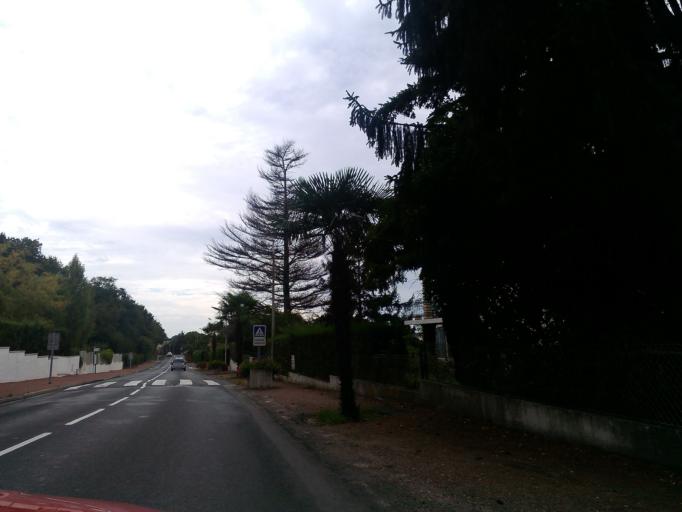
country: FR
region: Poitou-Charentes
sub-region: Departement de la Charente-Maritime
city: Breuillet
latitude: 45.6895
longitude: -1.0565
